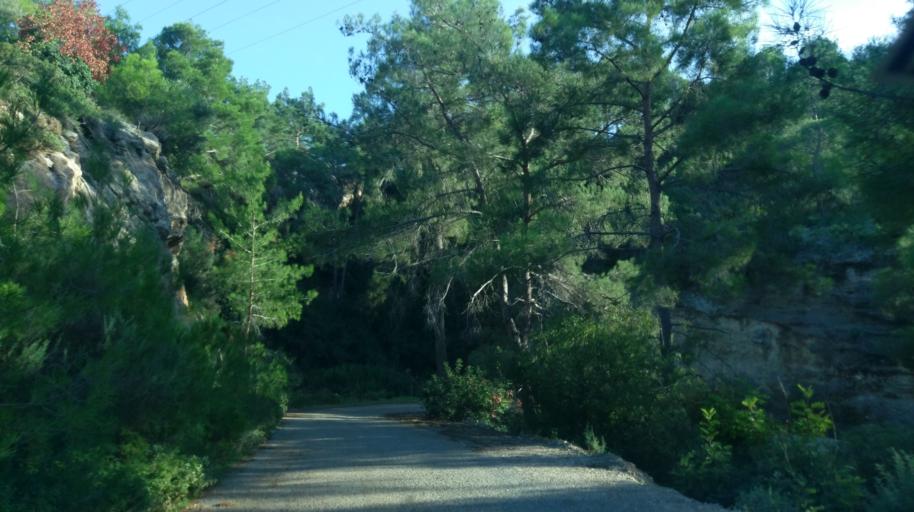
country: CY
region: Ammochostos
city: Lefkonoiko
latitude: 35.3286
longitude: 33.6006
